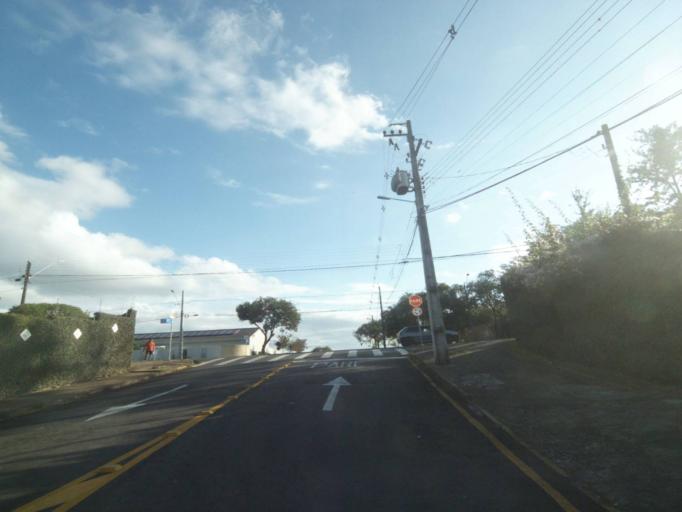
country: BR
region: Parana
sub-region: Telemaco Borba
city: Telemaco Borba
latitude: -24.3303
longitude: -50.6130
